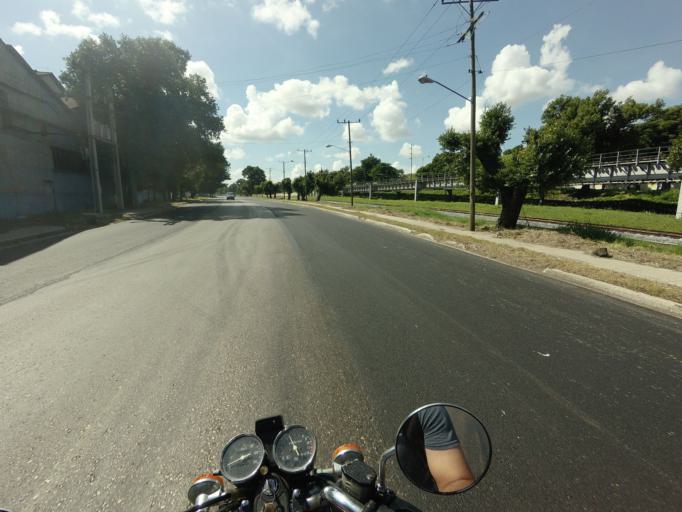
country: CU
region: La Habana
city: La Habana Vieja
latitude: 23.1215
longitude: -82.3598
